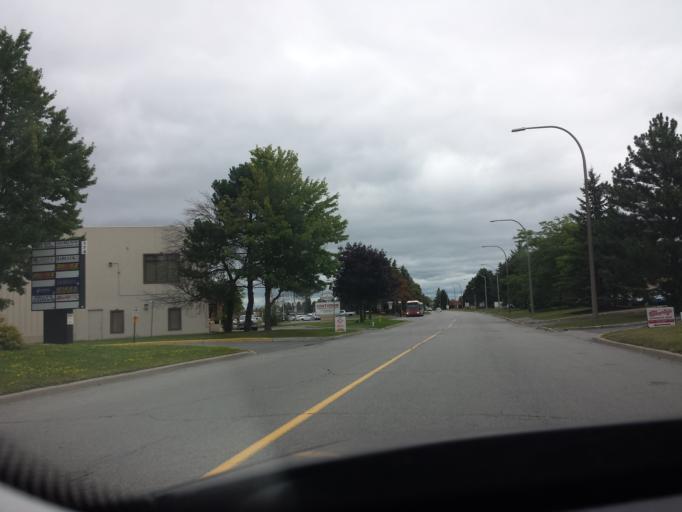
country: CA
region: Ontario
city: Ottawa
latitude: 45.3418
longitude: -75.7131
